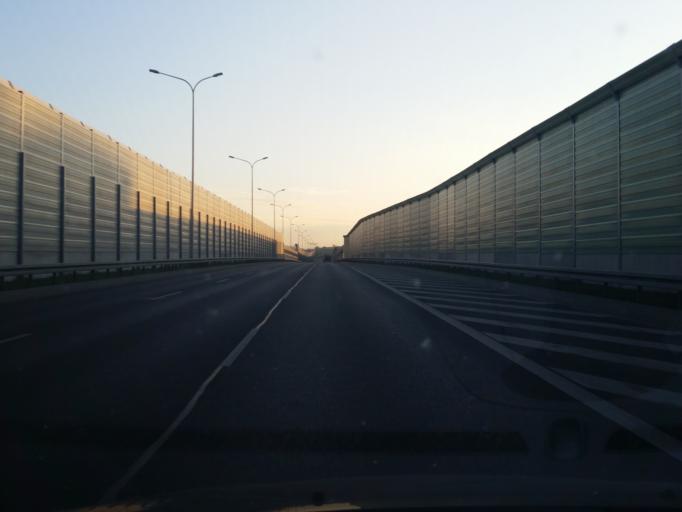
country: PL
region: Masovian Voivodeship
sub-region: Warszawa
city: Bialoleka
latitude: 52.3139
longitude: 20.9684
